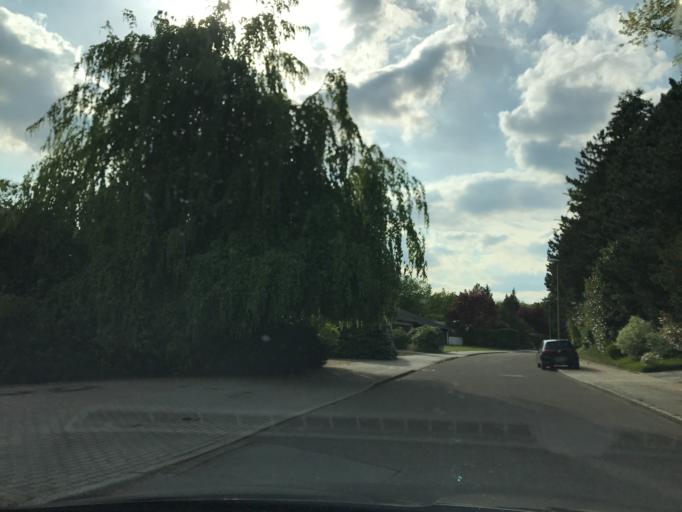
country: DE
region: North Rhine-Westphalia
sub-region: Regierungsbezirk Dusseldorf
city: Essen
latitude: 51.4033
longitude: 6.9772
